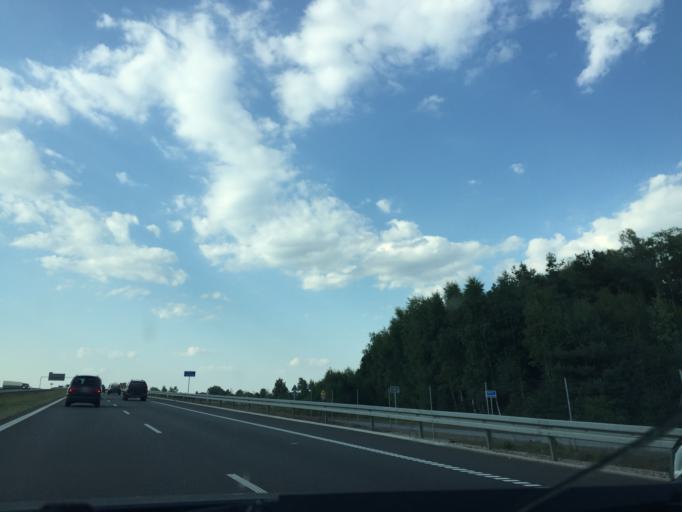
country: PL
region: Masovian Voivodeship
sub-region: Powiat szydlowiecki
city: Oronsko
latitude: 51.3475
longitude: 21.0153
